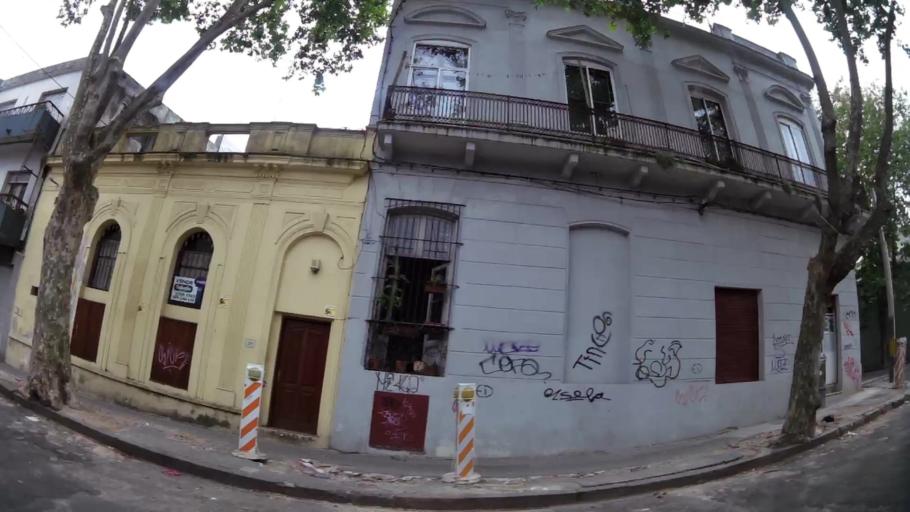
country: UY
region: Montevideo
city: Montevideo
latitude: -34.9100
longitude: -56.1830
